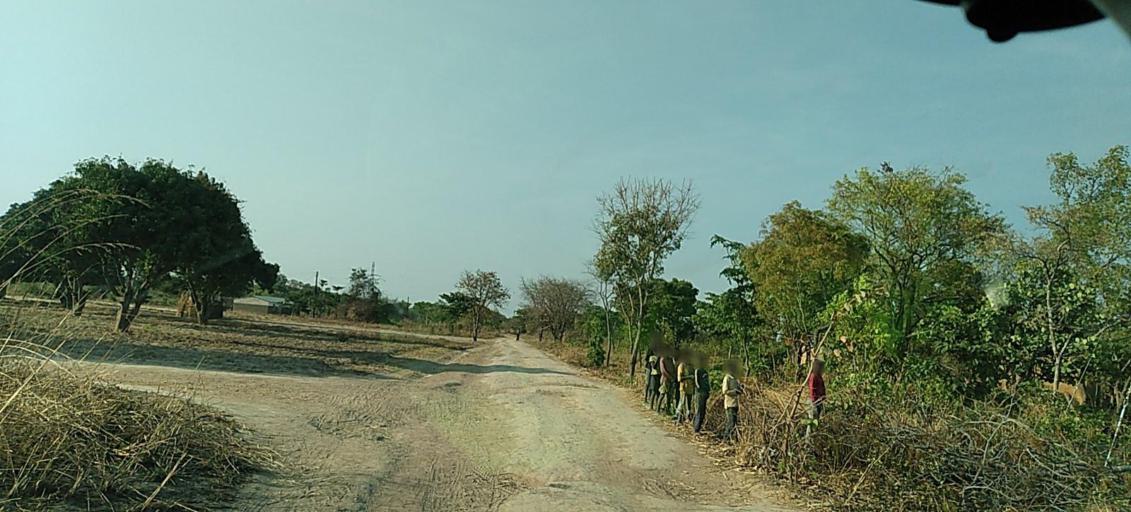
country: ZM
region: North-Western
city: Kalengwa
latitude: -13.1489
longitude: 25.0340
